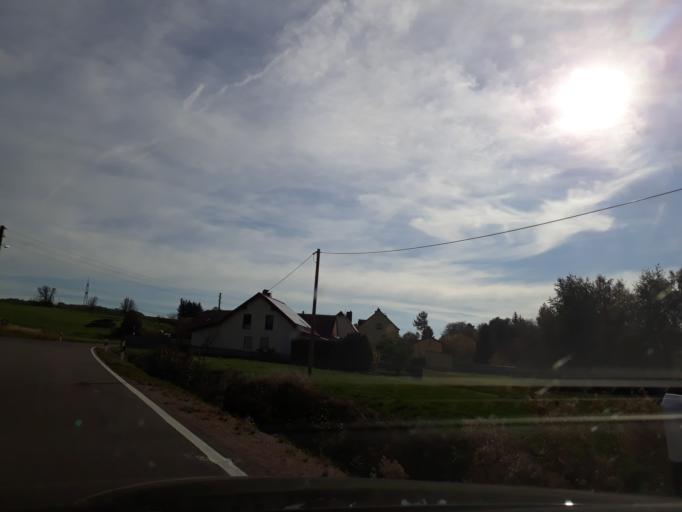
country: DE
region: Saxony
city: Niederstriegis
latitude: 51.1131
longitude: 13.1574
